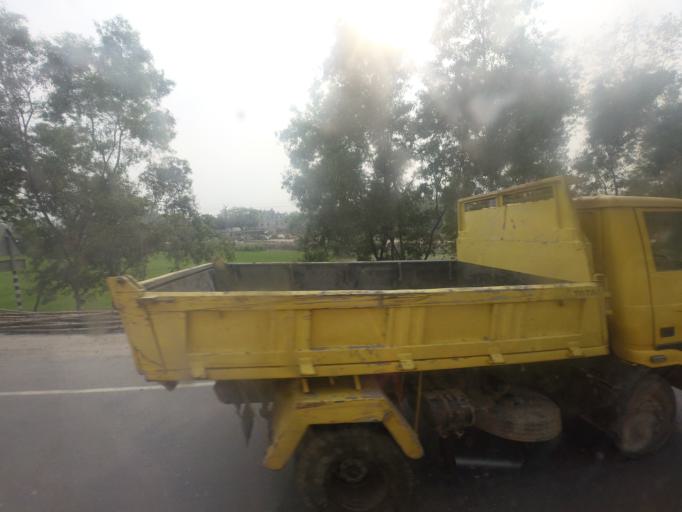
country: BD
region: Dhaka
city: Tangail
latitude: 24.3432
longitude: 89.9219
